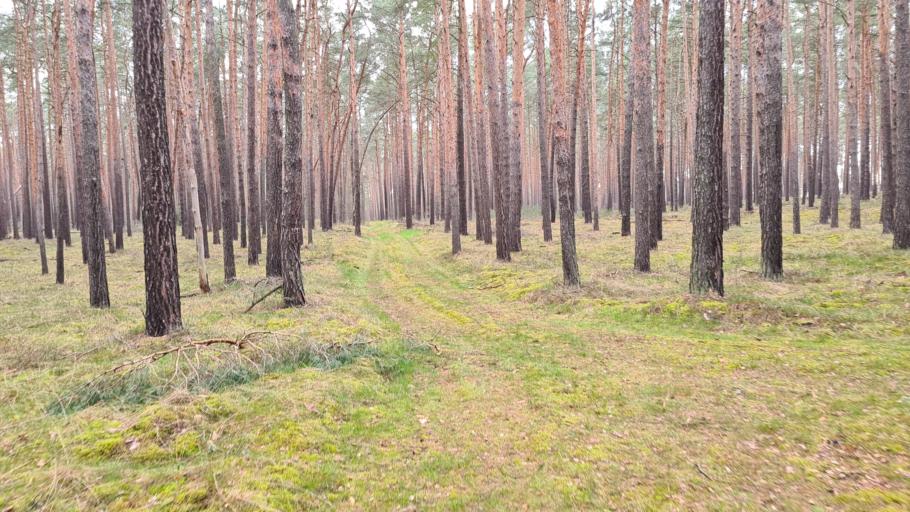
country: DE
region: Brandenburg
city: Schilda
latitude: 51.5602
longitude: 13.3846
